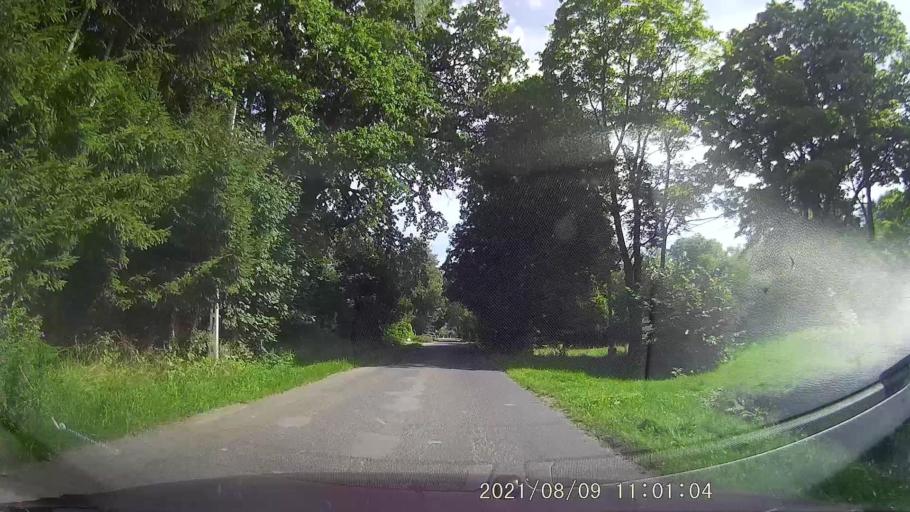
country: PL
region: Lower Silesian Voivodeship
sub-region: Powiat klodzki
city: Bozkow
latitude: 50.4585
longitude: 16.5515
